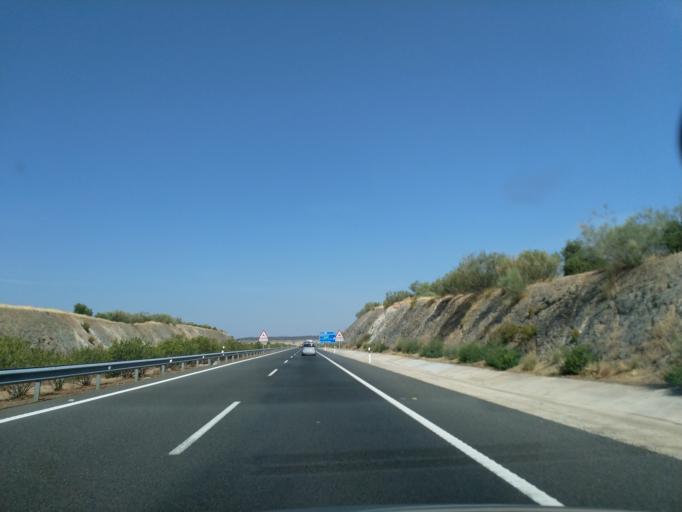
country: ES
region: Extremadura
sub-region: Provincia de Badajoz
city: Aljucen
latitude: 39.0282
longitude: -6.3341
